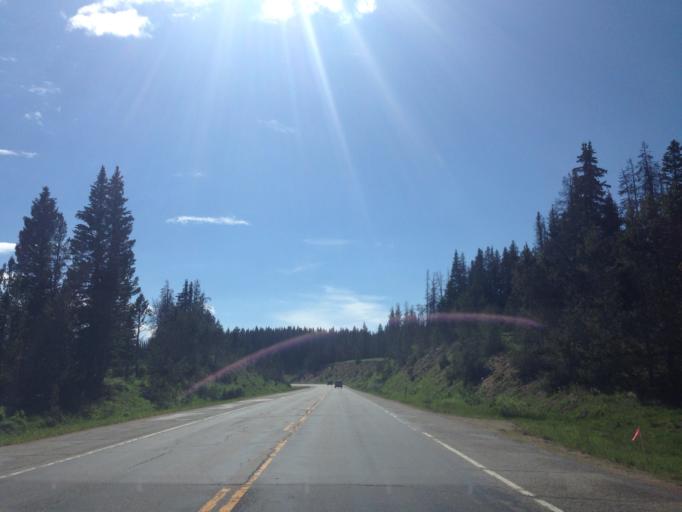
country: US
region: Colorado
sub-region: Routt County
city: Steamboat Springs
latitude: 40.3891
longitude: -106.6716
